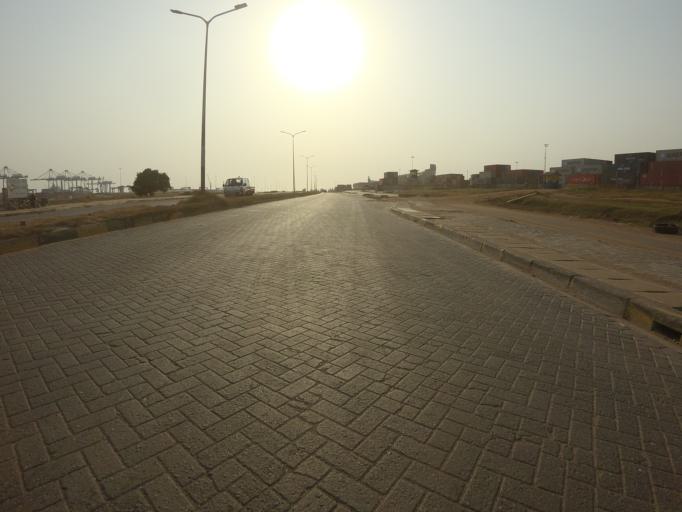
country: GH
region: Greater Accra
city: Tema
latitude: 5.6237
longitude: -0.0080
